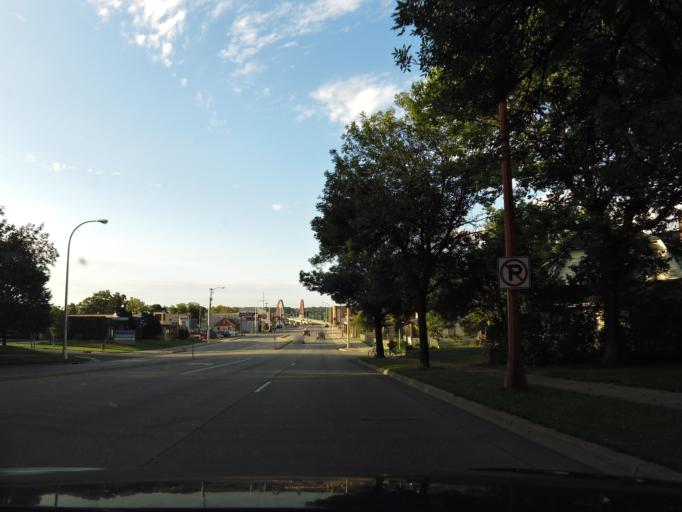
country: US
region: Minnesota
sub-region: Dakota County
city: Hastings
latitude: 44.7397
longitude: -92.8525
